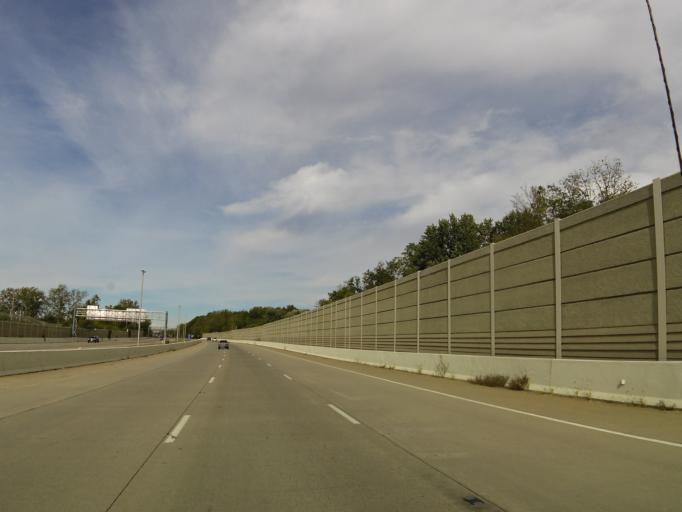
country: US
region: Indiana
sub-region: Marion County
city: Speedway
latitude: 39.8089
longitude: -86.2803
